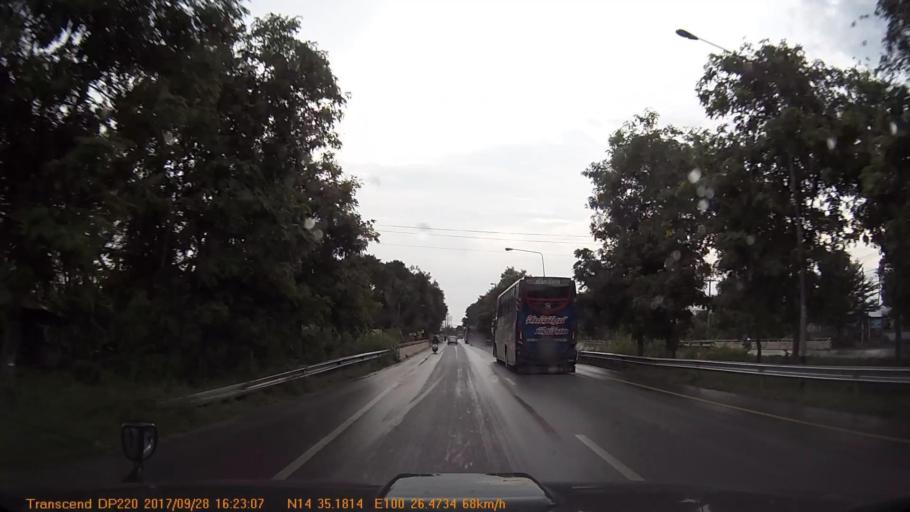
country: TH
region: Ang Thong
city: Ang Thong
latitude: 14.5872
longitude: 100.4410
